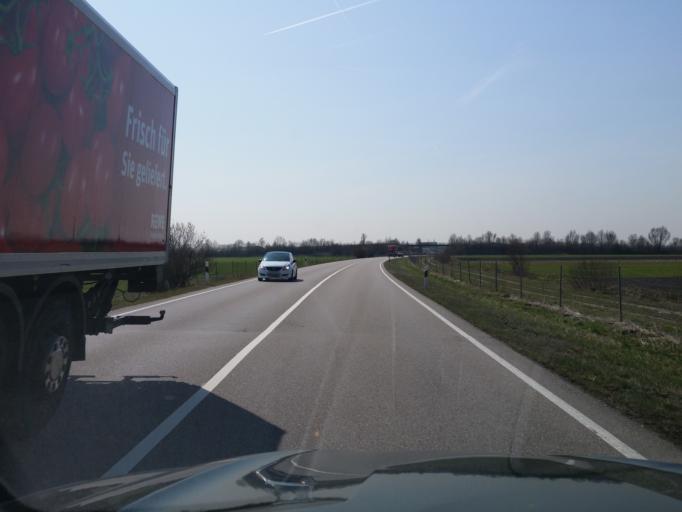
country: DE
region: Bavaria
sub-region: Upper Bavaria
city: Eitting
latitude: 48.3821
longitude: 11.8608
